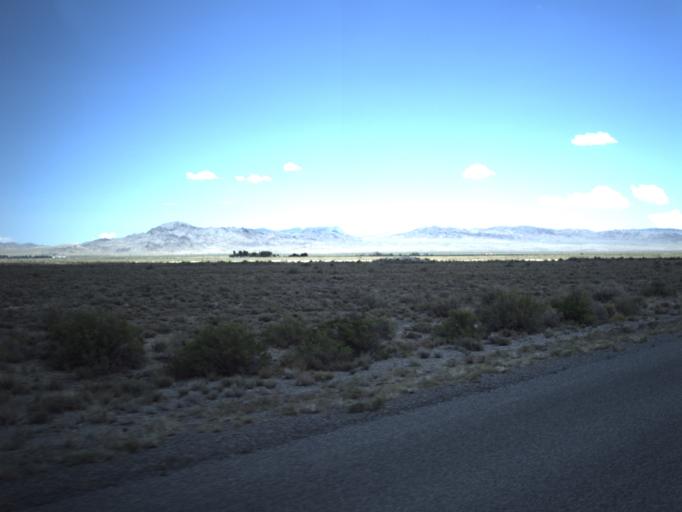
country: US
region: Nevada
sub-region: White Pine County
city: McGill
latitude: 39.0537
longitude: -114.0043
